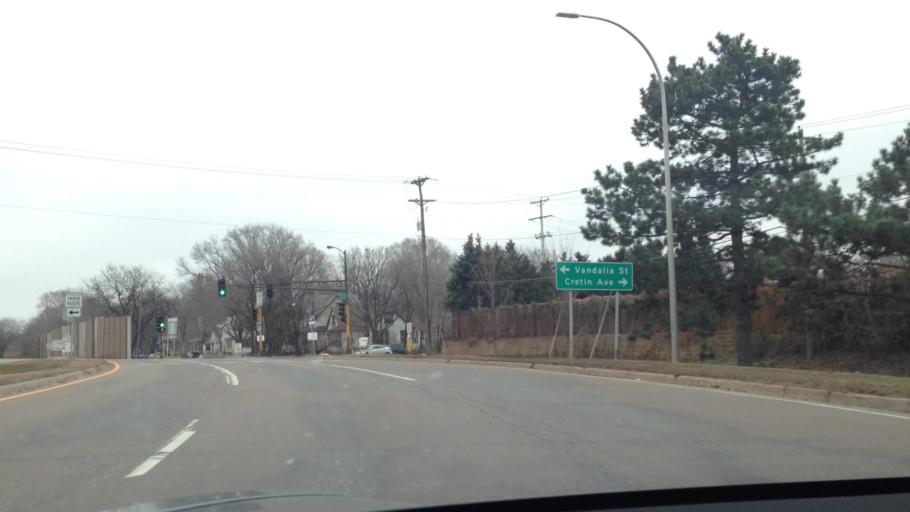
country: US
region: Minnesota
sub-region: Ramsey County
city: Lauderdale
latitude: 44.9557
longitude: -93.1934
